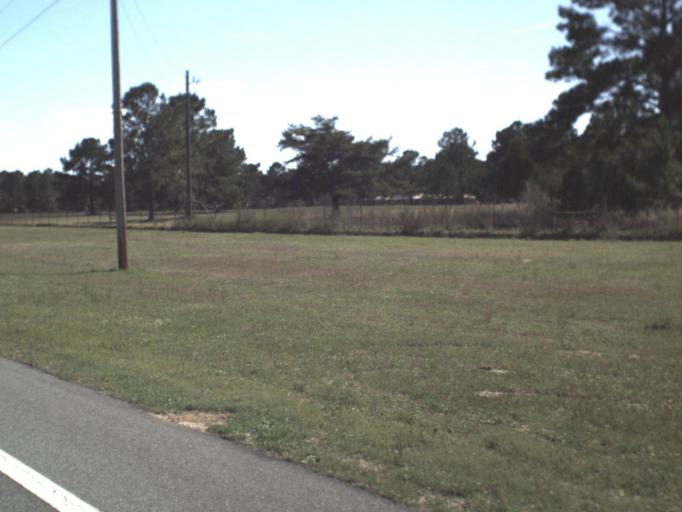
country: US
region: Florida
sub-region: Gadsden County
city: Gretna
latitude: 30.6771
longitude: -84.7062
